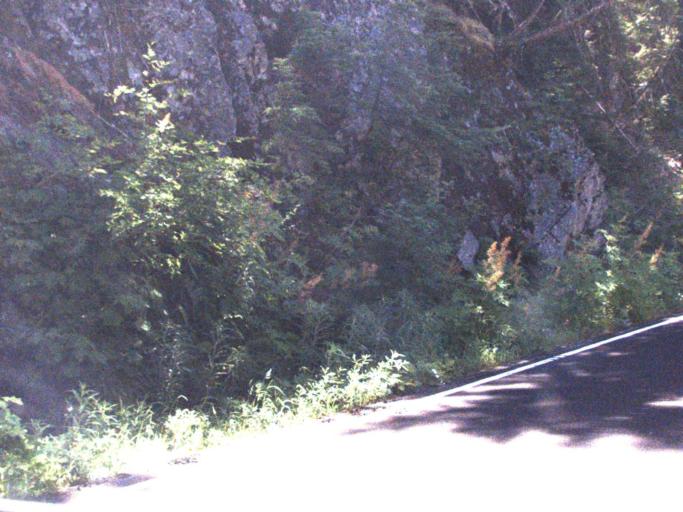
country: US
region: Washington
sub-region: King County
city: Enumclaw
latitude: 46.8252
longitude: -121.5444
